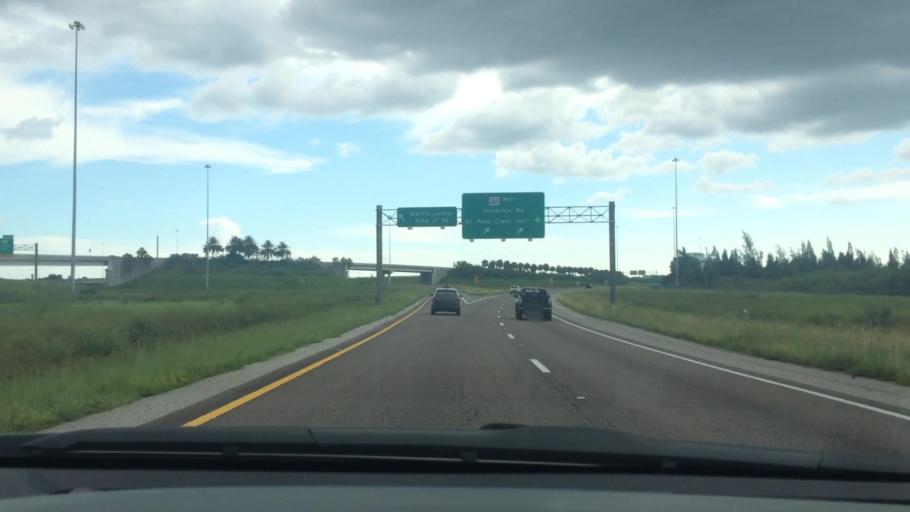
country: US
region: Florida
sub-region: Pinellas County
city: Feather Sound
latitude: 27.8959
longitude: -82.6439
